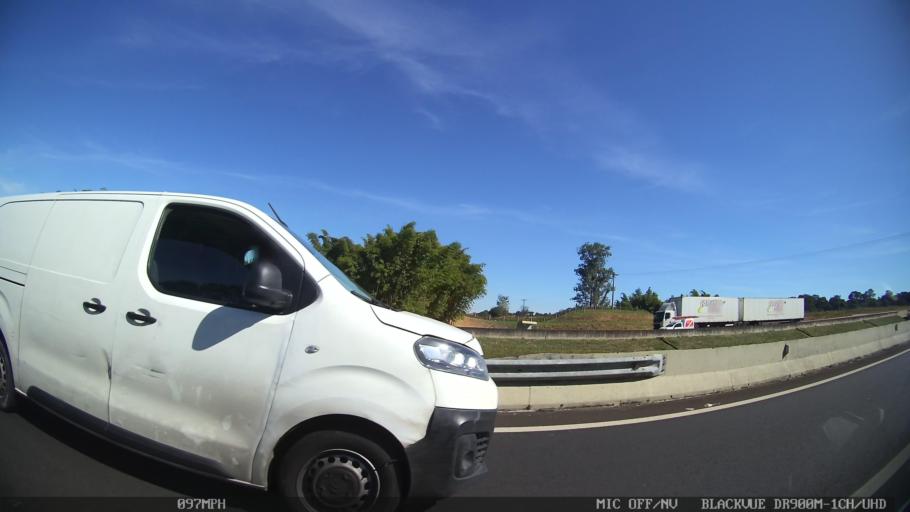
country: BR
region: Sao Paulo
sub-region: Santa Rita Do Passa Quatro
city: Santa Rita do Passa Quatro
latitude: -21.7305
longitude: -47.5847
